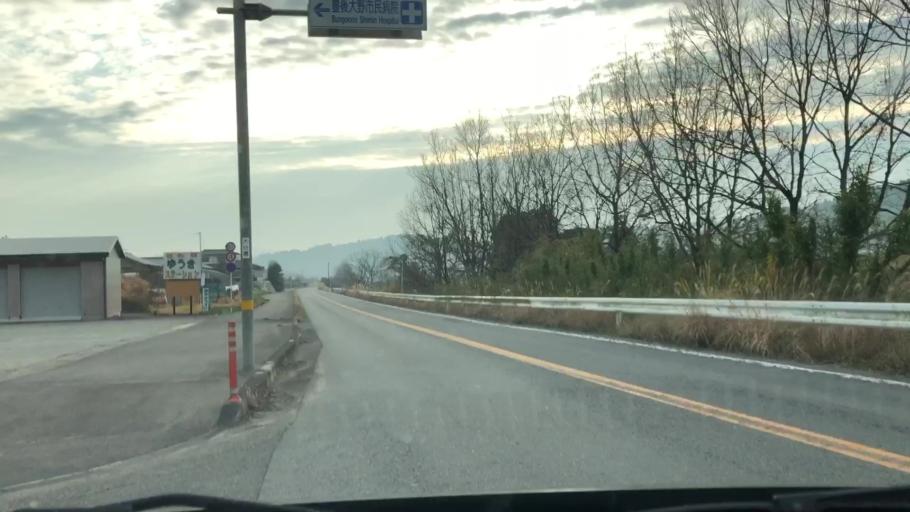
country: JP
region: Oita
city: Takedamachi
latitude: 32.9688
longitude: 131.4751
